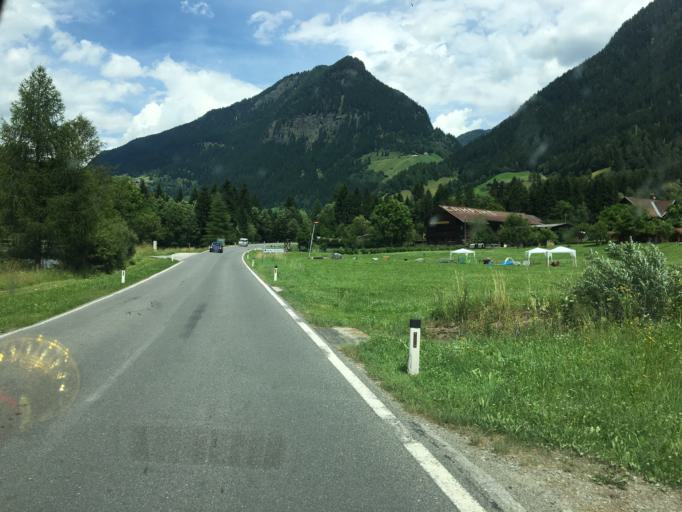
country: AT
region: Carinthia
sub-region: Politischer Bezirk Spittal an der Drau
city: Mortschach
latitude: 46.9080
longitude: 12.9097
